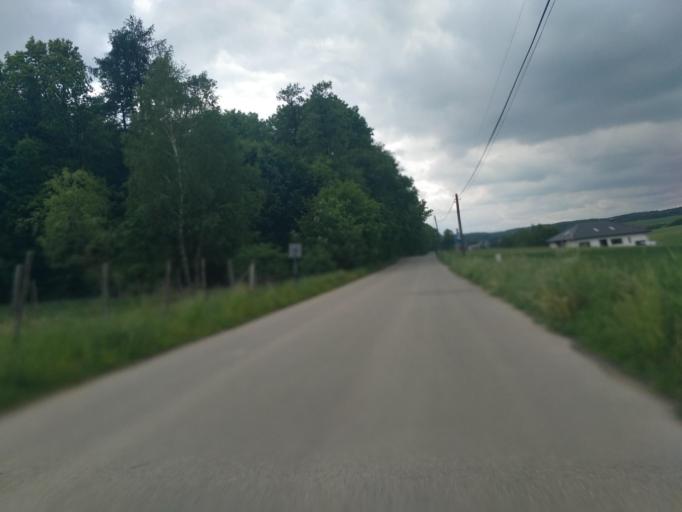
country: PL
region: Subcarpathian Voivodeship
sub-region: Powiat jasielski
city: Tarnowiec
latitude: 49.6613
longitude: 21.5650
